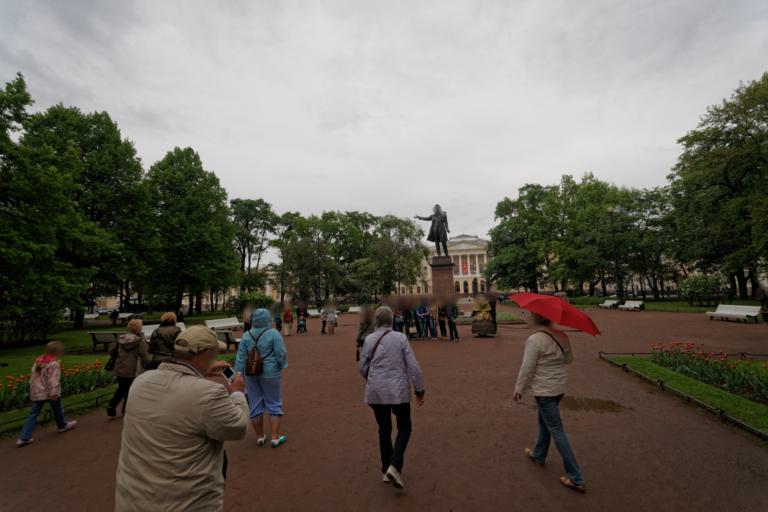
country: RU
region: St.-Petersburg
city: Saint Petersburg
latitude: 59.9370
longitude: 30.3316
